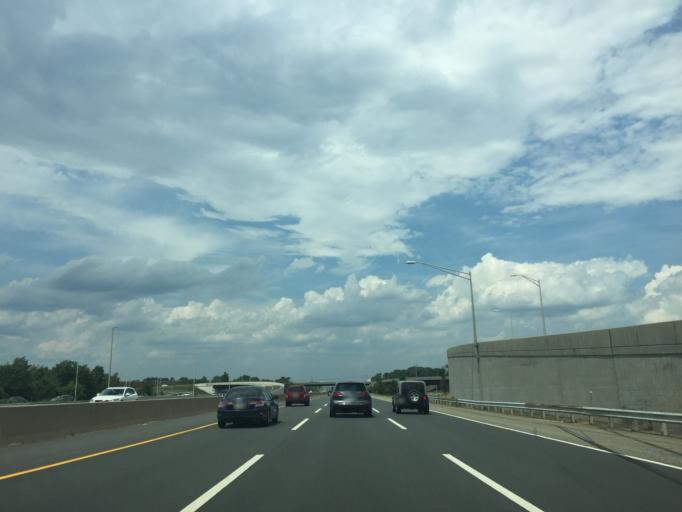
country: US
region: New Jersey
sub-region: Middlesex County
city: Rossmoor
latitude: 40.3473
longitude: -74.4749
